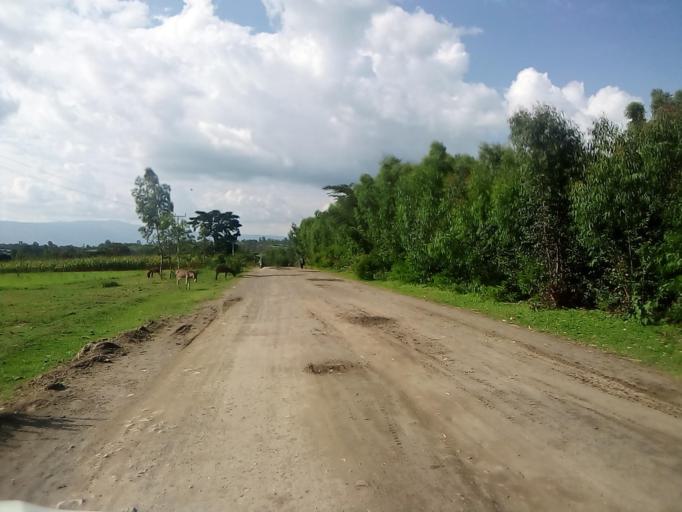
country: ET
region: Southern Nations, Nationalities, and People's Region
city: K'olito
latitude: 7.6568
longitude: 38.0483
